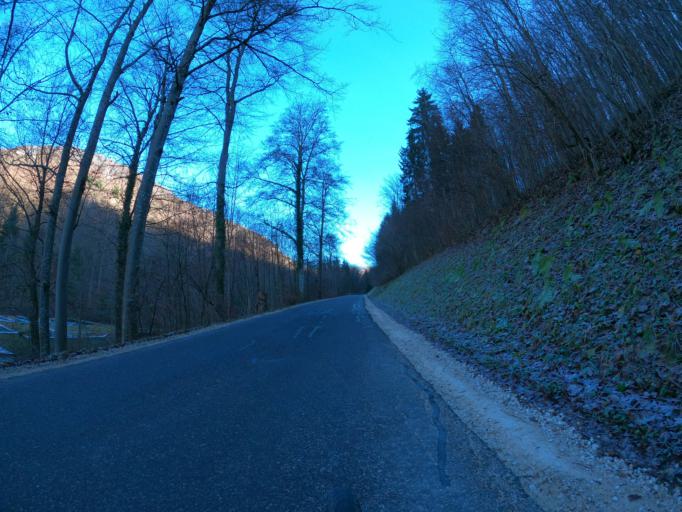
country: DE
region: Baden-Wuerttemberg
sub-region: Tuebingen Region
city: Eningen unter Achalm
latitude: 48.4478
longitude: 9.2828
